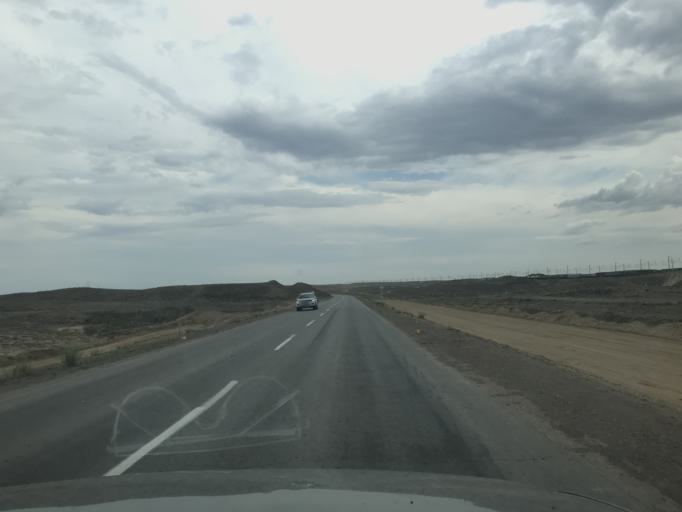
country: KZ
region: Almaty Oblysy
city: Ulken
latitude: 44.9866
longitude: 74.0094
